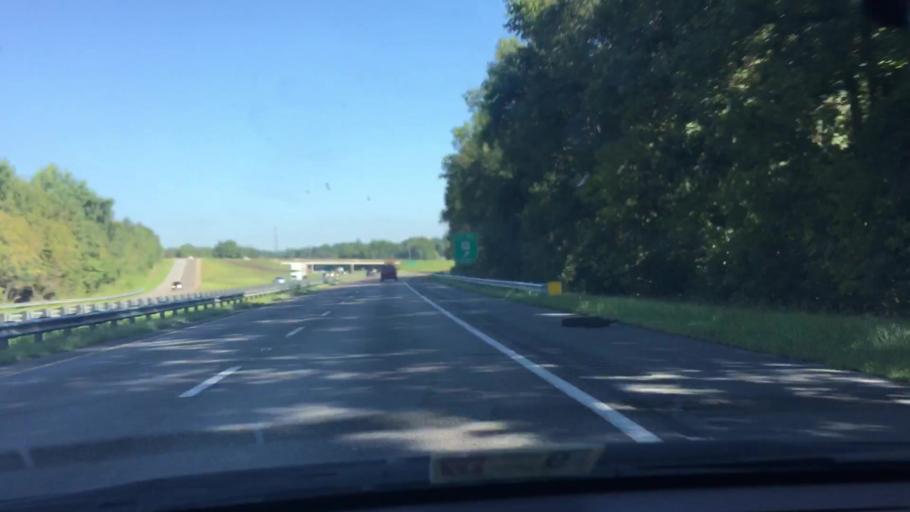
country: US
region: North Carolina
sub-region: Iredell County
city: Statesville
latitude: 35.8443
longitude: -80.8591
